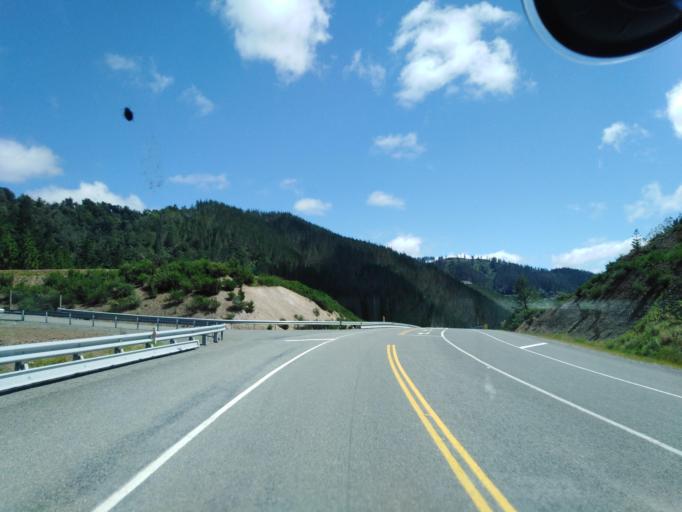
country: NZ
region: Nelson
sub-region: Nelson City
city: Nelson
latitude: -41.1909
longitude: 173.5543
